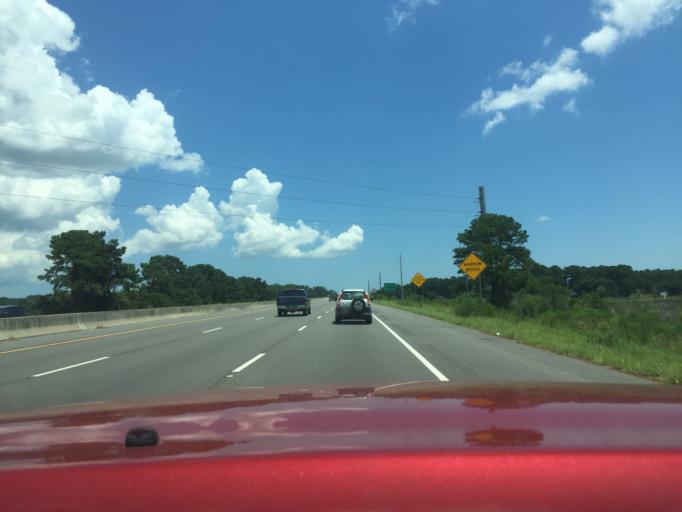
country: US
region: Georgia
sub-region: Chatham County
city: Georgetown
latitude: 31.9837
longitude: -81.1871
